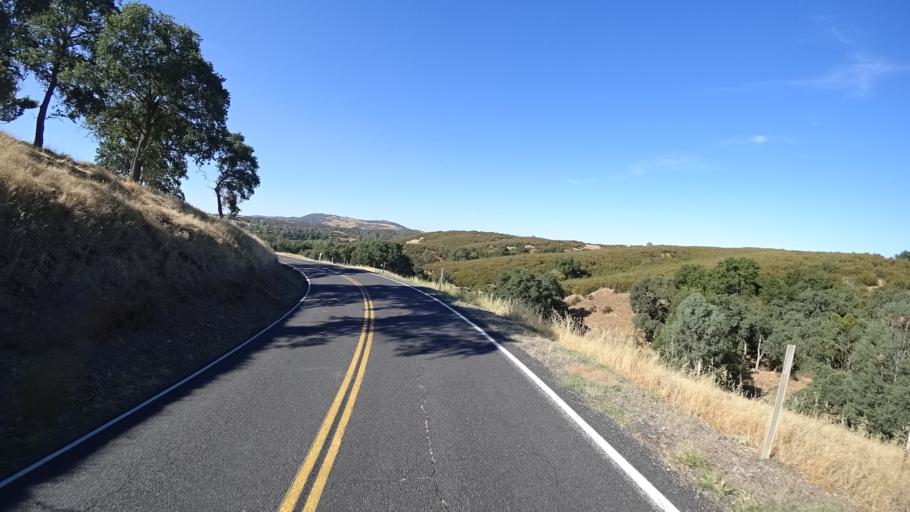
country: US
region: California
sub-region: Calaveras County
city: Valley Springs
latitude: 38.1581
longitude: -120.8179
